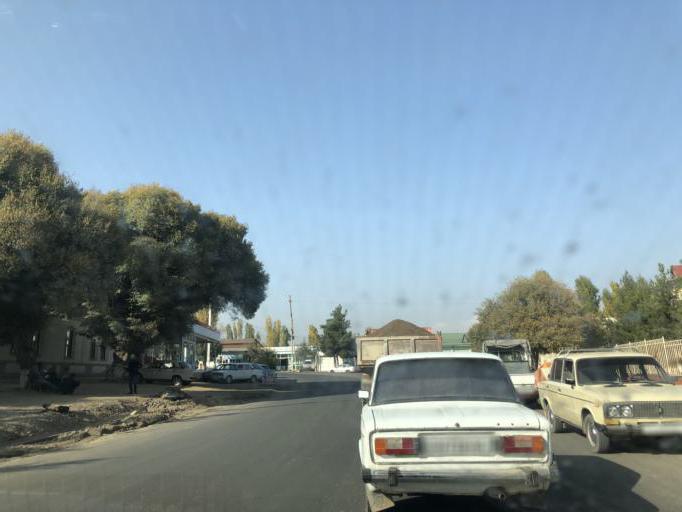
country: UZ
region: Namangan
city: Chust Shahri
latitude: 41.0727
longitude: 71.2044
